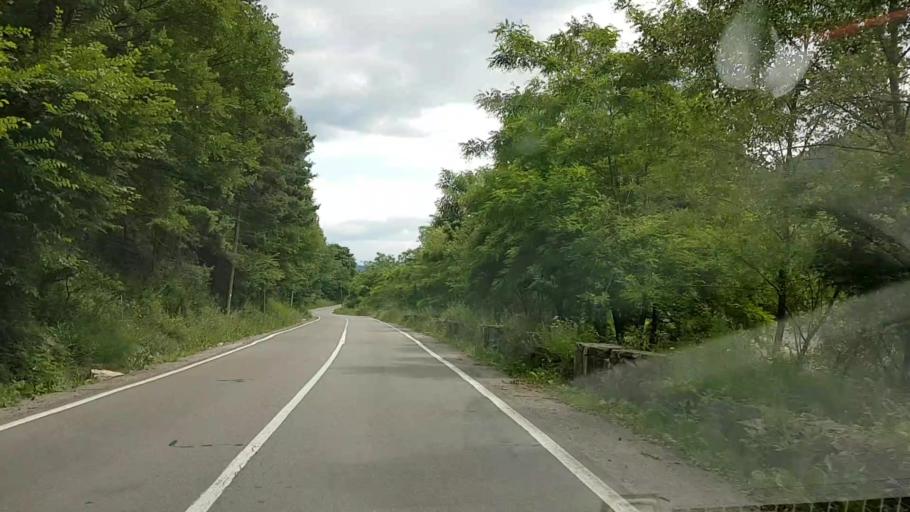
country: RO
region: Neamt
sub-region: Comuna Poiana Teiului
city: Poiana Teiului
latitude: 47.1223
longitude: 25.9084
